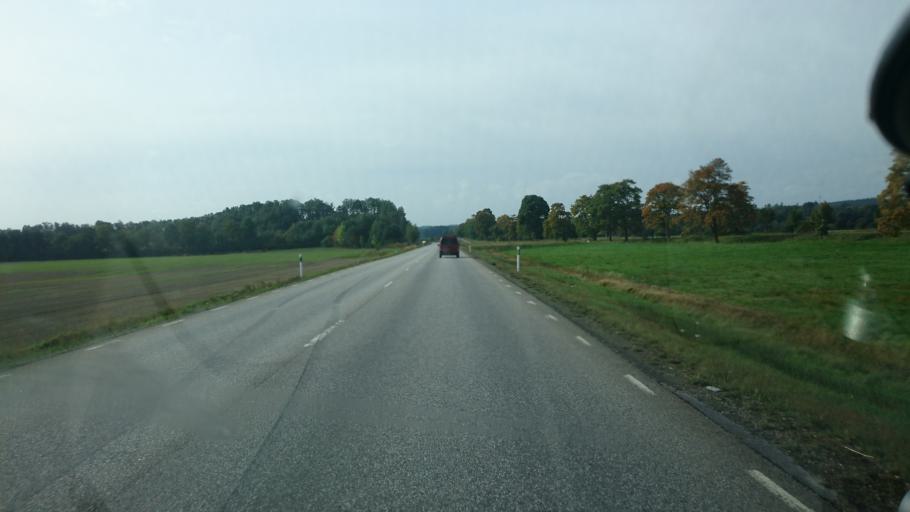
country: SE
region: Vaestra Goetaland
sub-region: Alingsas Kommun
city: Sollebrunn
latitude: 58.1060
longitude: 12.5173
